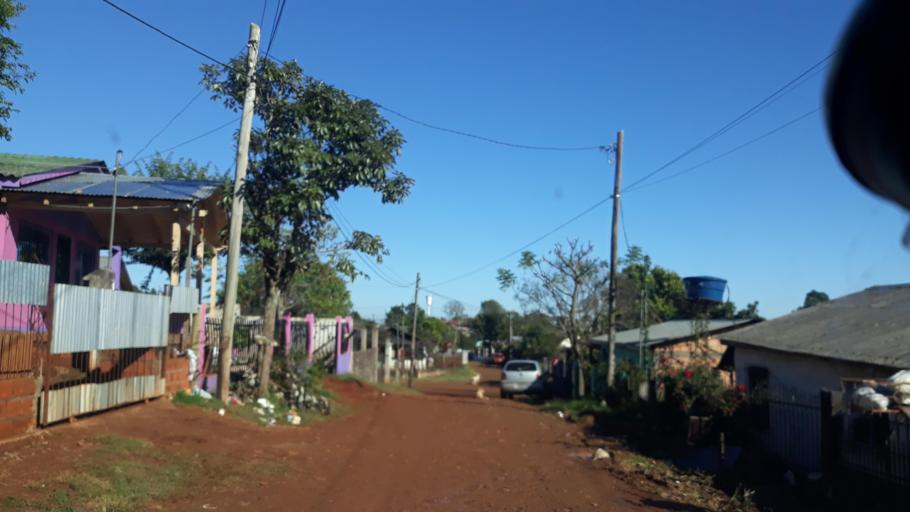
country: AR
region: Misiones
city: Bernardo de Irigoyen
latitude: -26.2616
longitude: -53.6534
